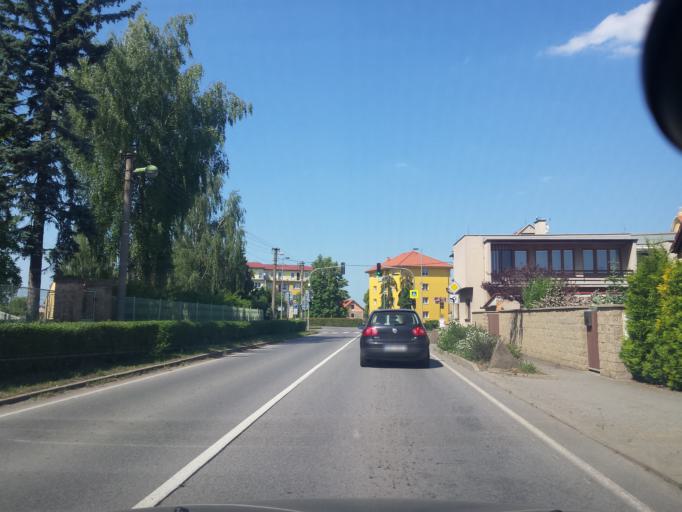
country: CZ
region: Central Bohemia
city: Velke Prilepy
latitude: 50.1906
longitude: 14.3217
